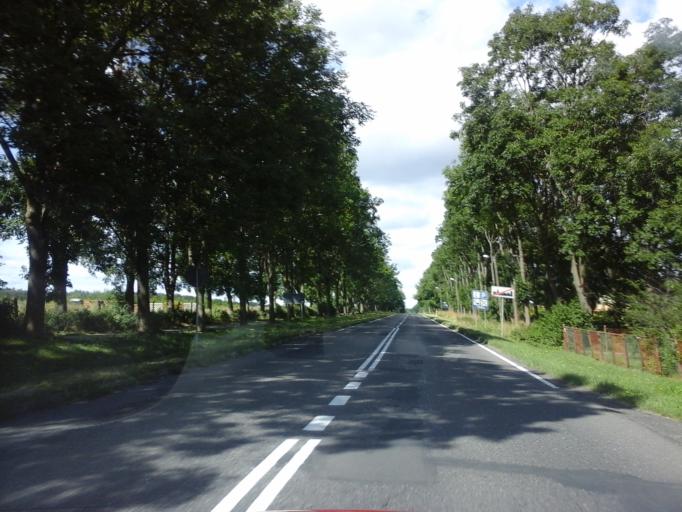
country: PL
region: West Pomeranian Voivodeship
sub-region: Powiat stargardzki
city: Kobylanka
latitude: 53.3458
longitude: 14.8658
